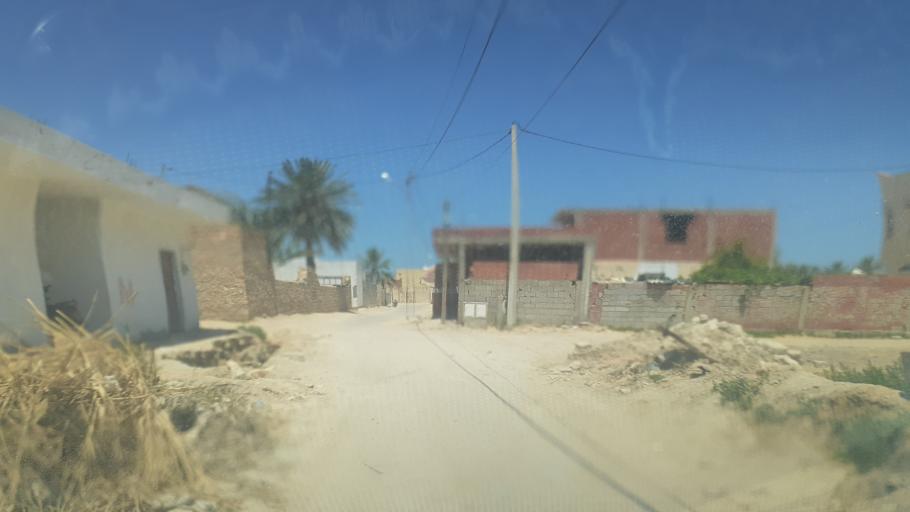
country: TN
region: Qabis
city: Gabes
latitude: 33.9322
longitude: 10.0596
